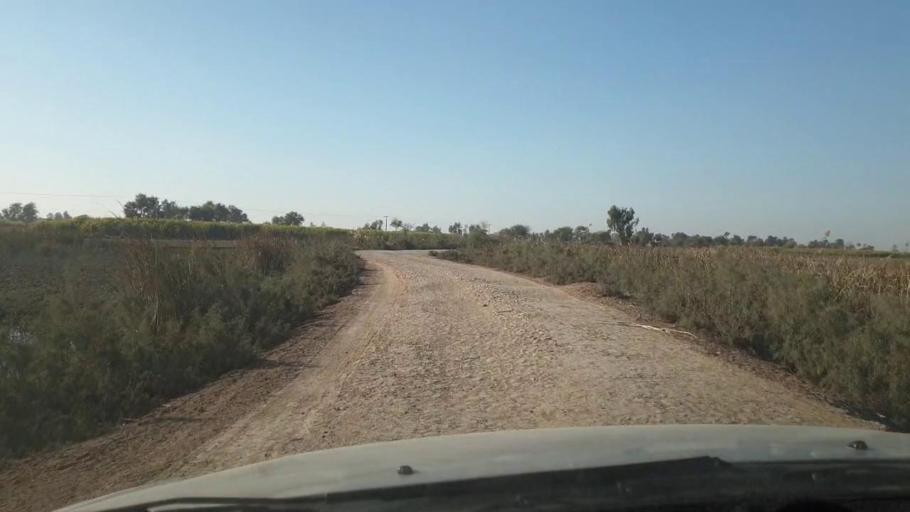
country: PK
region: Sindh
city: Ghotki
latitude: 28.0422
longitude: 69.2962
